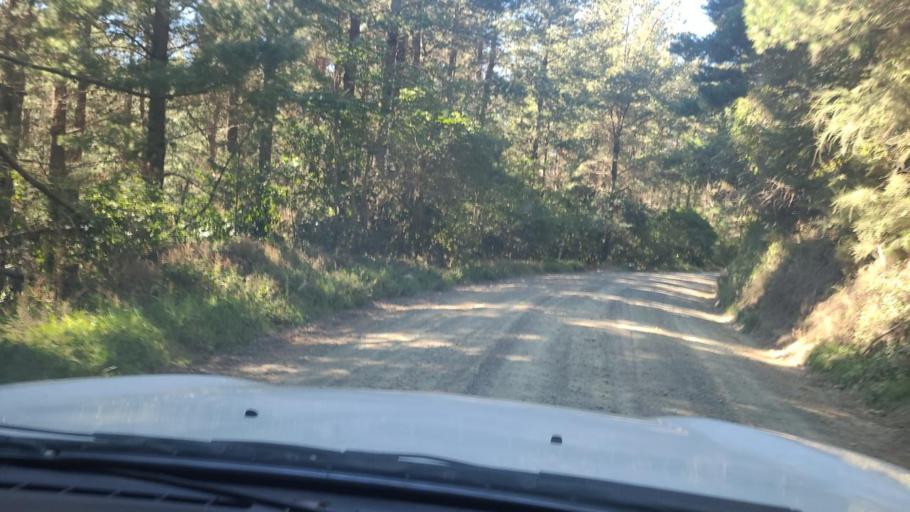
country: NZ
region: Hawke's Bay
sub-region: Napier City
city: Taradale
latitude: -39.4084
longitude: 176.4722
